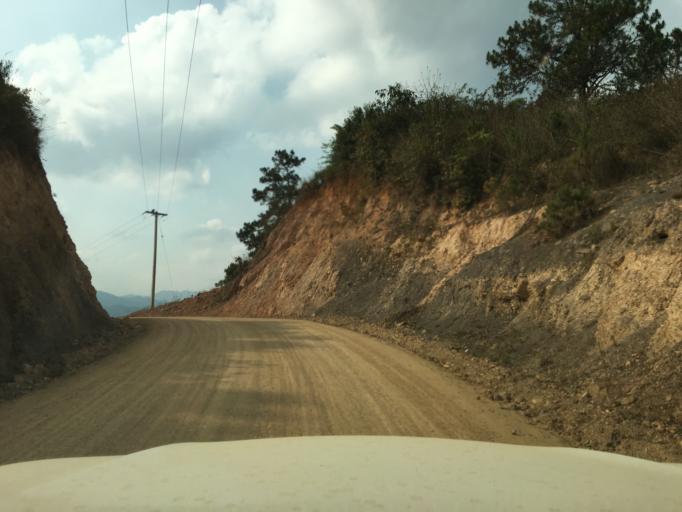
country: LA
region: Houaphan
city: Huameung
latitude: 20.2105
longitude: 103.8715
